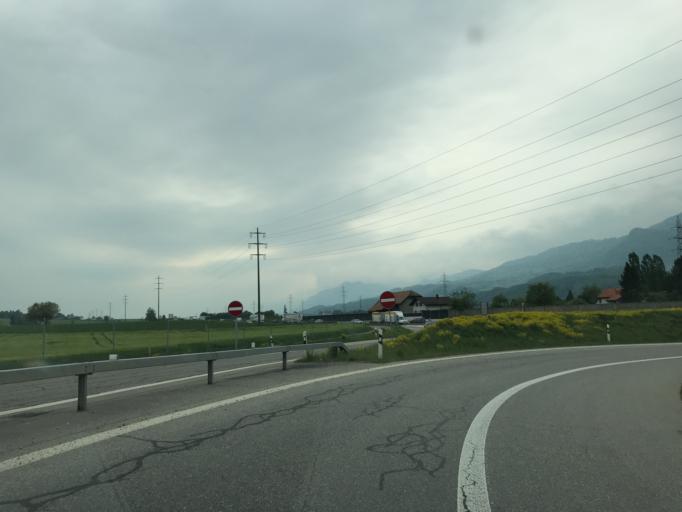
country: CH
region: Bern
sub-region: Oberaargau
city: Niederbipp
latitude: 47.2595
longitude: 7.7061
